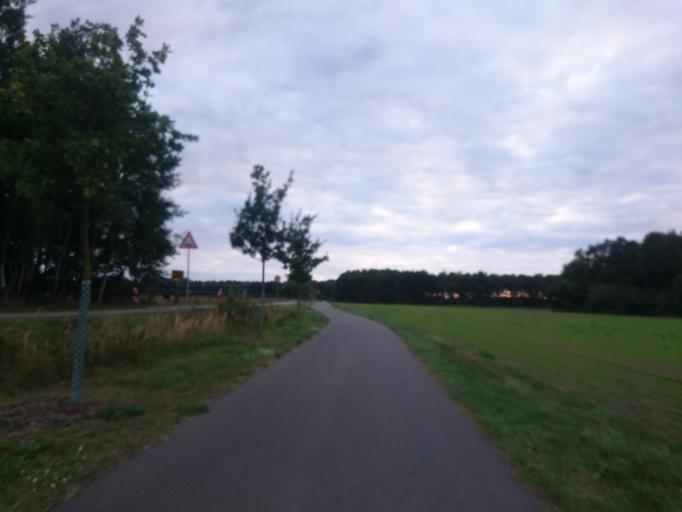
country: DE
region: Mecklenburg-Vorpommern
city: Zingst
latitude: 54.3766
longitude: 12.6521
